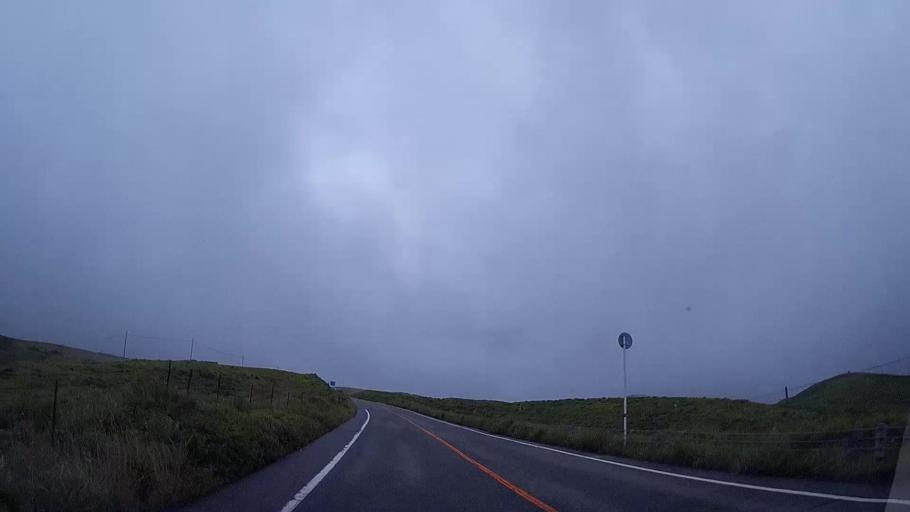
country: JP
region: Kumamoto
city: Aso
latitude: 33.0051
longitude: 131.0698
